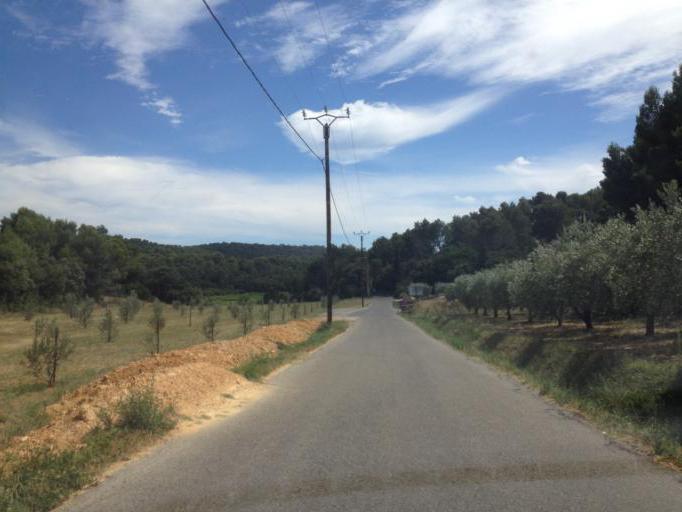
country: FR
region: Provence-Alpes-Cote d'Azur
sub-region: Departement du Vaucluse
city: Malaucene
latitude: 44.1530
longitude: 5.1015
